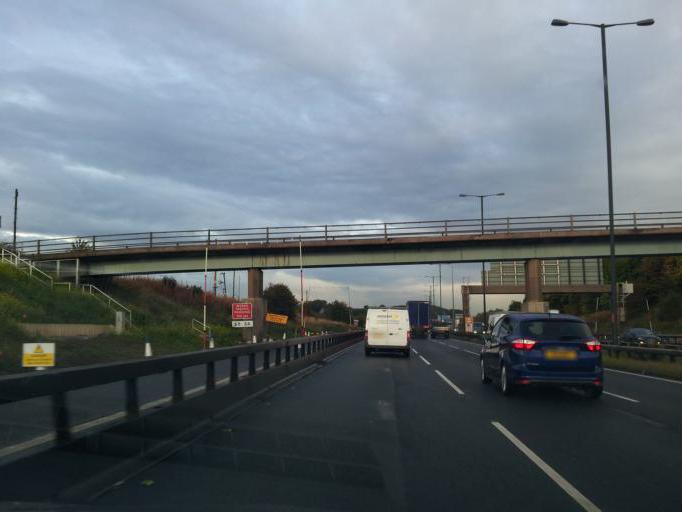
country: GB
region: England
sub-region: Manchester
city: Crumpsall
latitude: 53.5590
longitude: -2.2459
